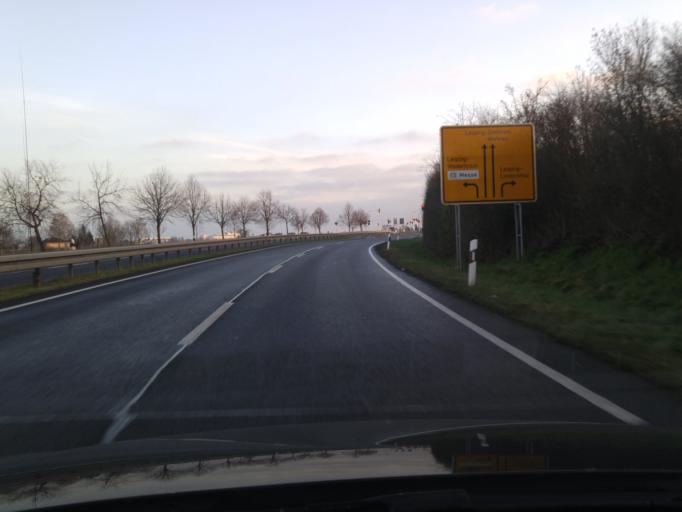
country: DE
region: Saxony
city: Rackwitz
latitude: 51.3954
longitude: 12.3419
